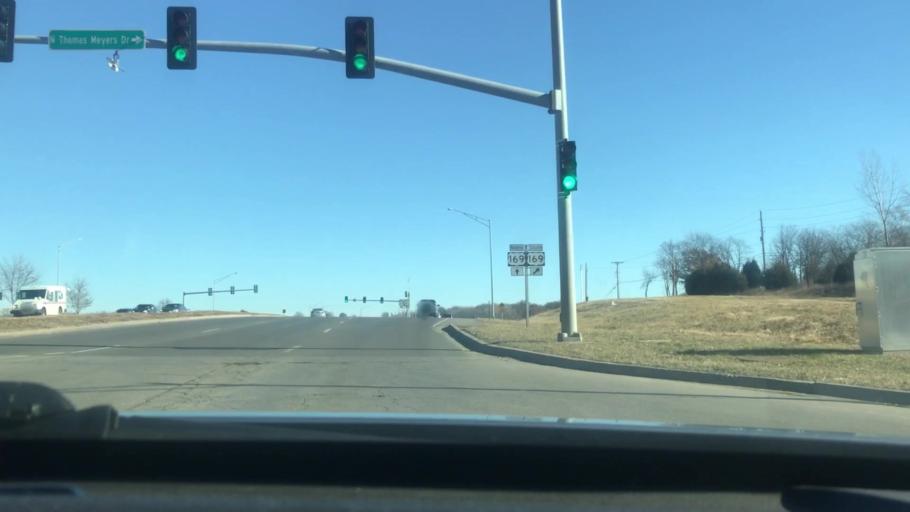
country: US
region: Missouri
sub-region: Clay County
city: Gladstone
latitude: 39.2463
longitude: -94.5945
